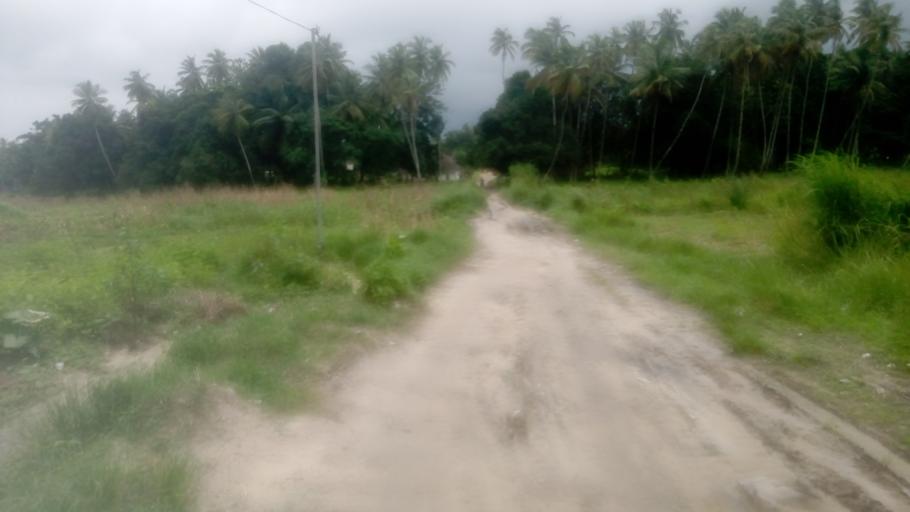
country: SL
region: Northern Province
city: Lunsar
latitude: 8.6793
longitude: -12.5370
